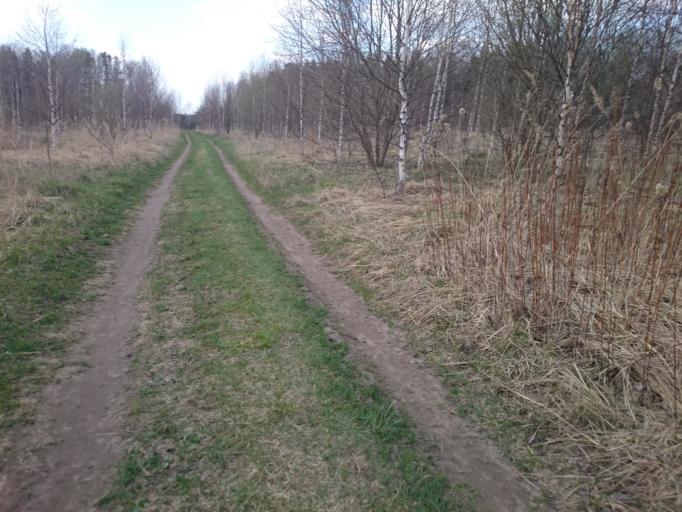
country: RU
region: Moskovskaya
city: Klin
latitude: 56.4023
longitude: 36.6802
